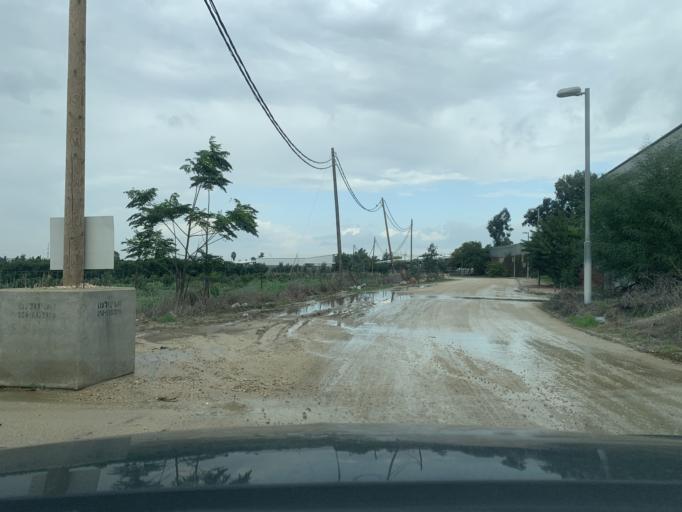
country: PS
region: West Bank
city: Qalqilyah
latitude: 32.2067
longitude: 34.9785
